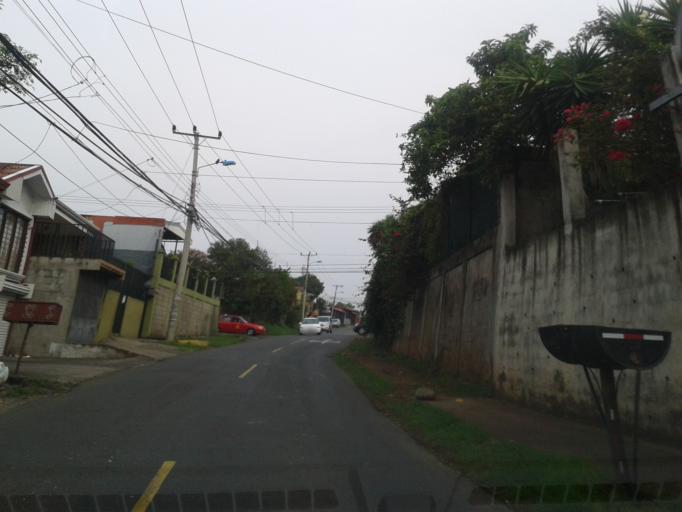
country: CR
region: Heredia
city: Mercedes
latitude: 10.0069
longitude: -84.1435
